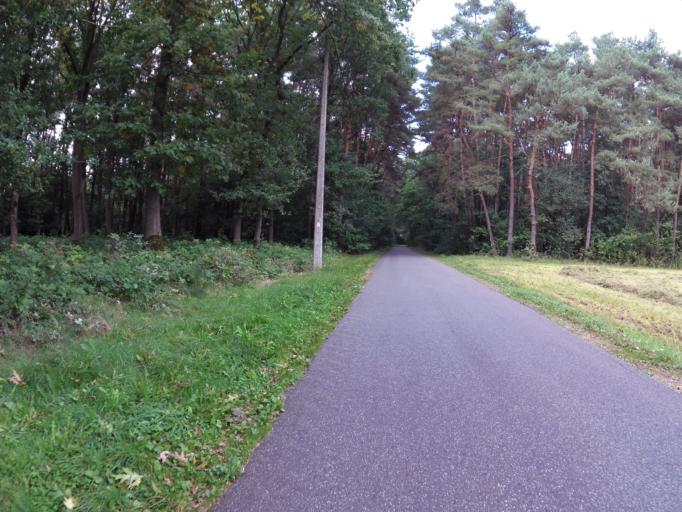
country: BE
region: Flanders
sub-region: Provincie Limburg
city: Zutendaal
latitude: 50.9139
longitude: 5.6105
